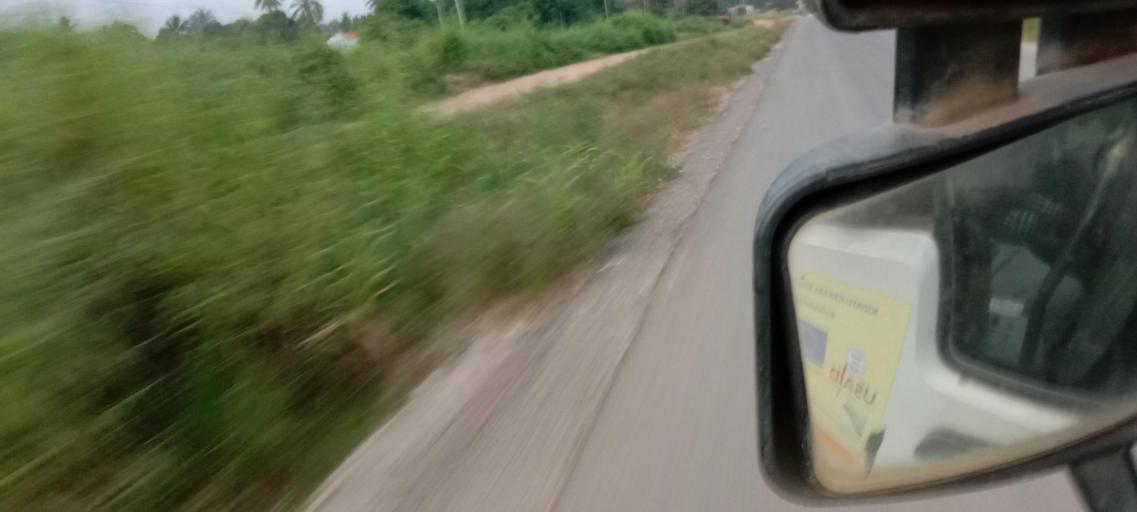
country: TZ
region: Morogoro
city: Ifakara
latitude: -7.9611
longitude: 36.8508
